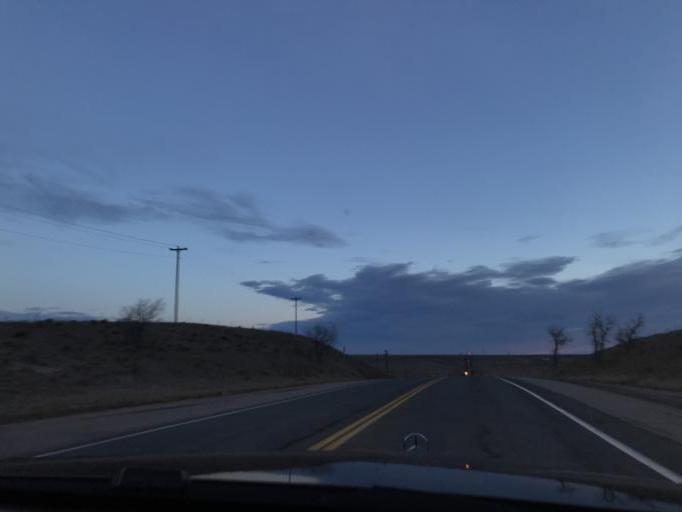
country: US
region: Colorado
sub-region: Boulder County
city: Superior
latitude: 39.8906
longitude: -105.1655
